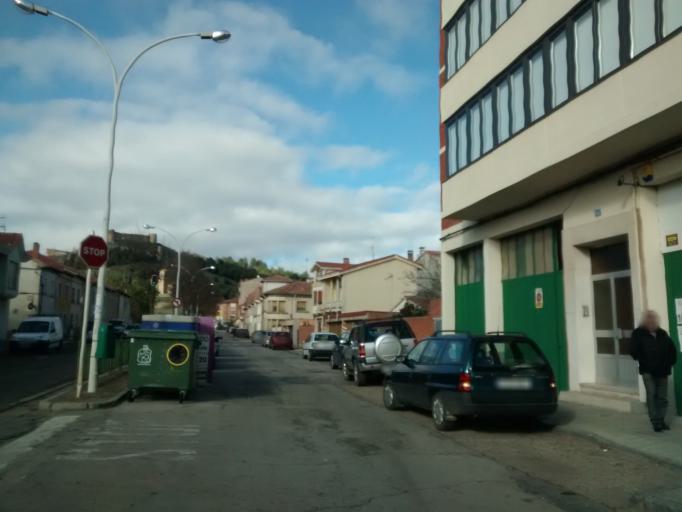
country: ES
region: Castille and Leon
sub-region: Provincia de Palencia
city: Aguilar de Campoo
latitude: 42.7940
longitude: -4.2574
